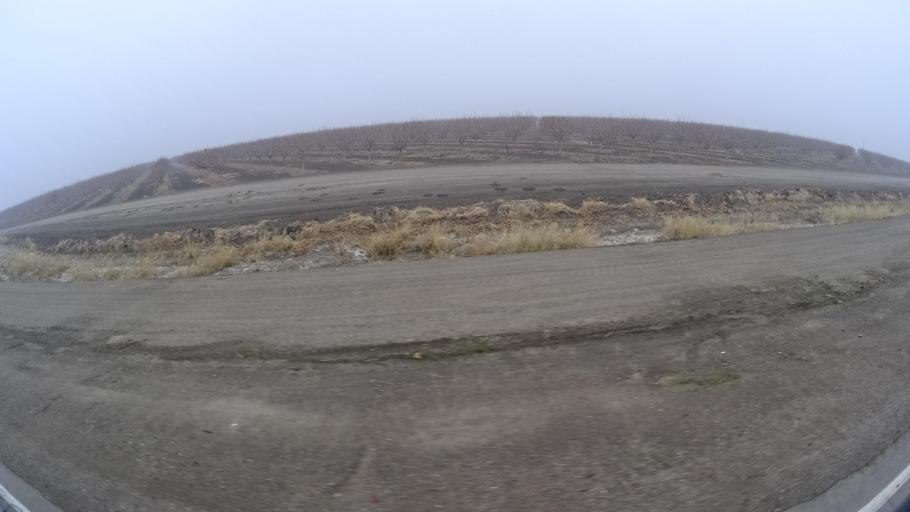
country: US
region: California
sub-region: Kern County
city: Lost Hills
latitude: 35.5041
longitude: -119.6058
